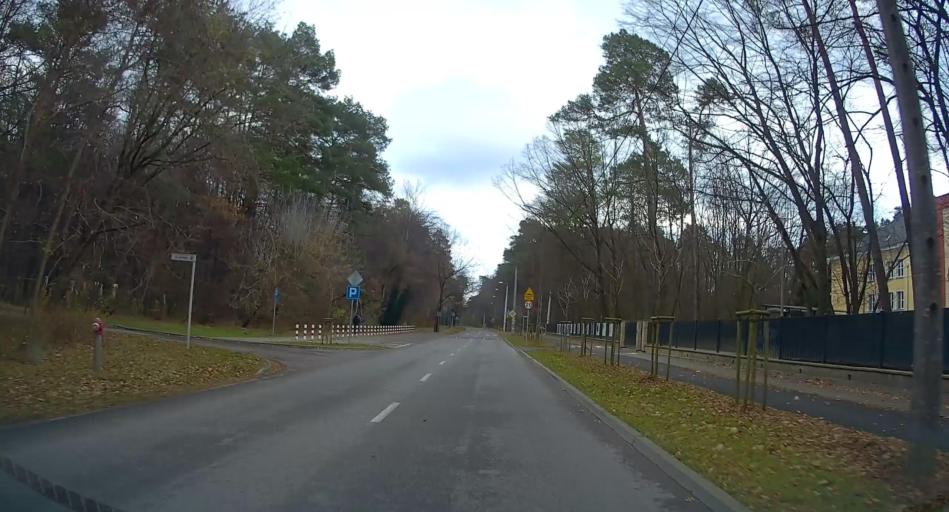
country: PL
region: Masovian Voivodeship
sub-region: Powiat piaseczynski
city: Piaseczno
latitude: 52.0593
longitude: 21.0145
